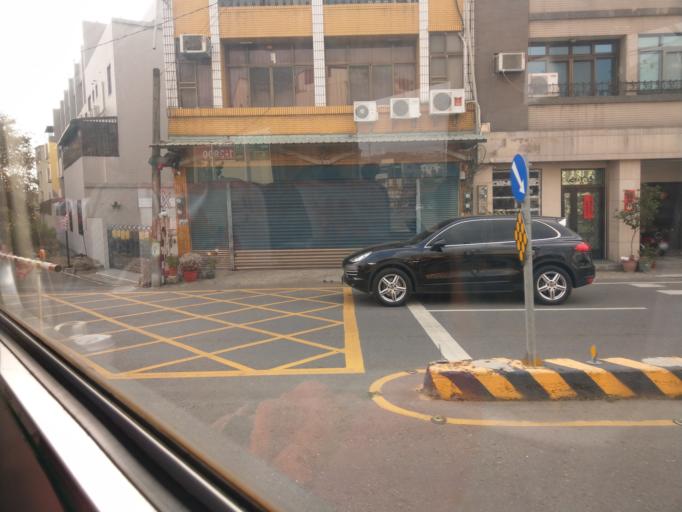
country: TW
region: Taiwan
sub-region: Chiayi
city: Jiayi Shi
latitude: 23.5196
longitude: 120.5485
